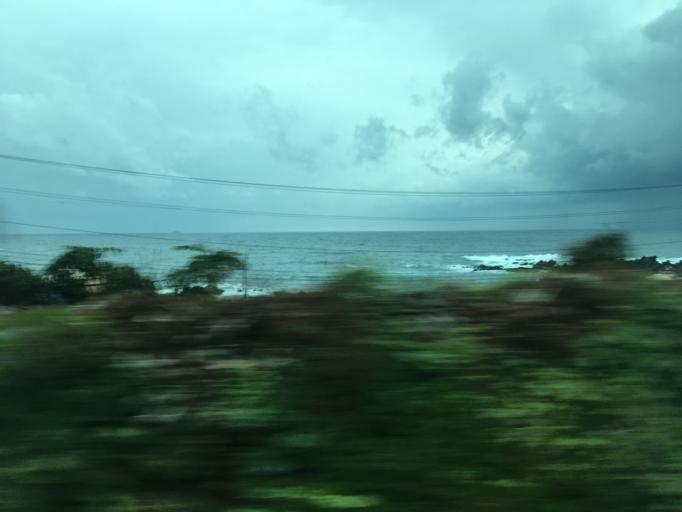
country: JP
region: Yamagata
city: Tsuruoka
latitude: 38.6010
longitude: 139.5713
